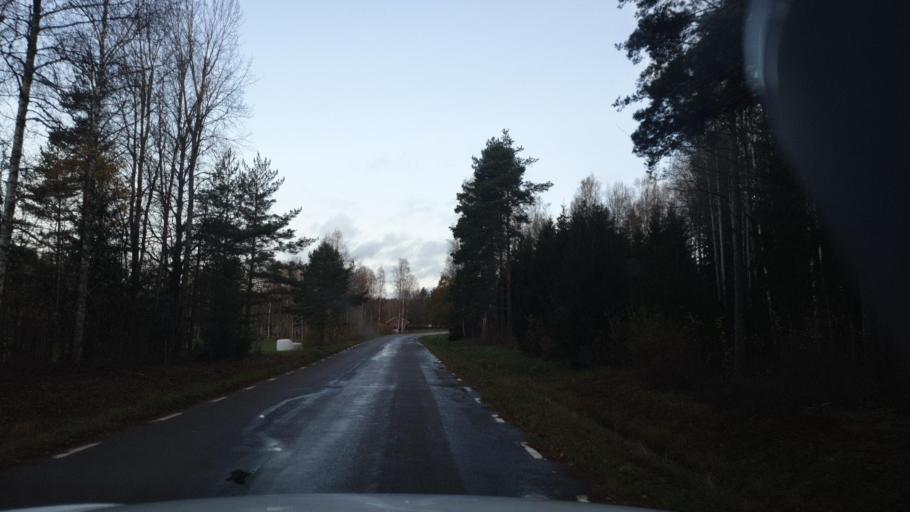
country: SE
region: Vaermland
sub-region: Arvika Kommun
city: Arvika
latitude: 59.5502
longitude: 12.7404
